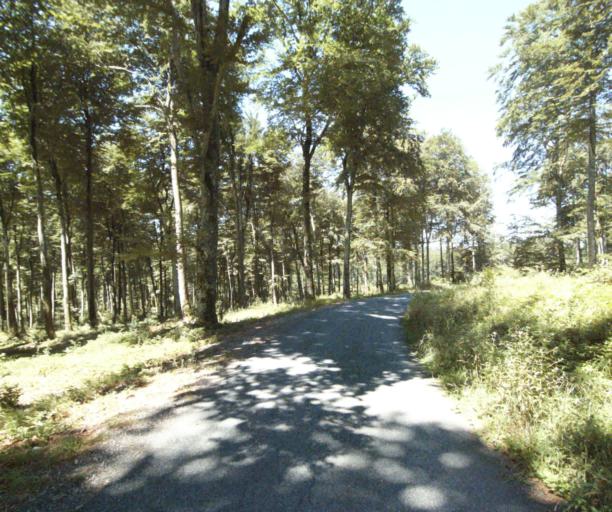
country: FR
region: Midi-Pyrenees
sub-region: Departement du Tarn
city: Dourgne
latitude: 43.4121
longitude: 2.1883
